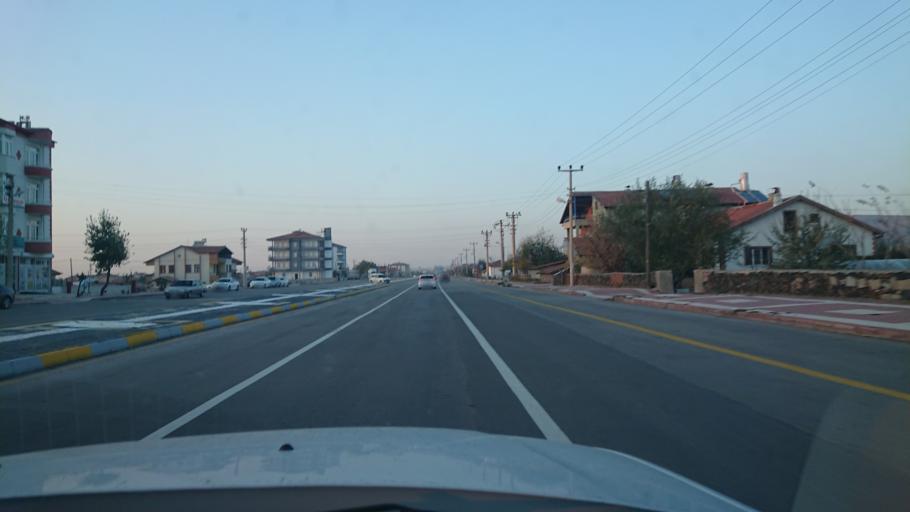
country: TR
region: Aksaray
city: Aksaray
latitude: 38.3370
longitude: 34.0481
